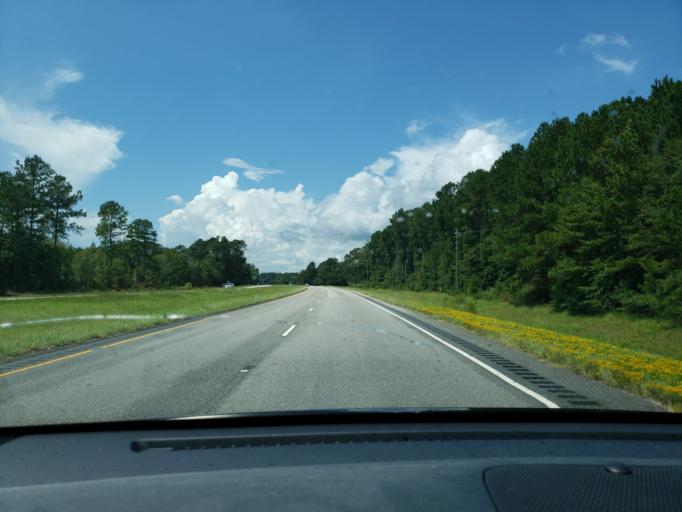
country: US
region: North Carolina
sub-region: Bladen County
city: Elizabethtown
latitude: 34.6434
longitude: -78.6791
